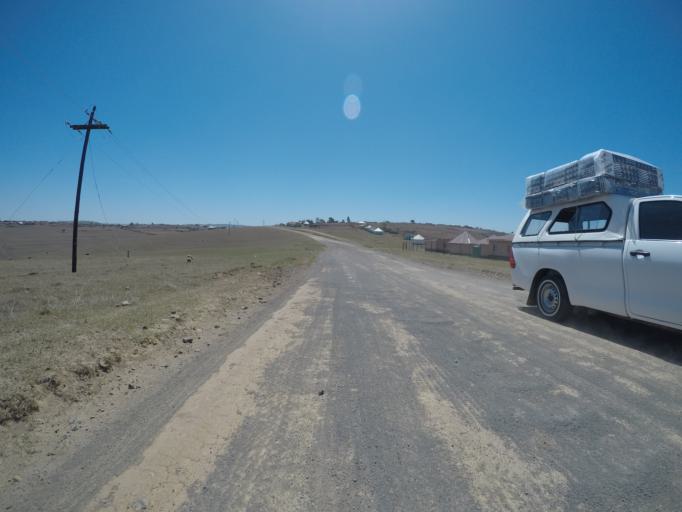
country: ZA
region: Eastern Cape
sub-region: OR Tambo District Municipality
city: Mthatha
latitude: -31.7888
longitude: 28.8166
